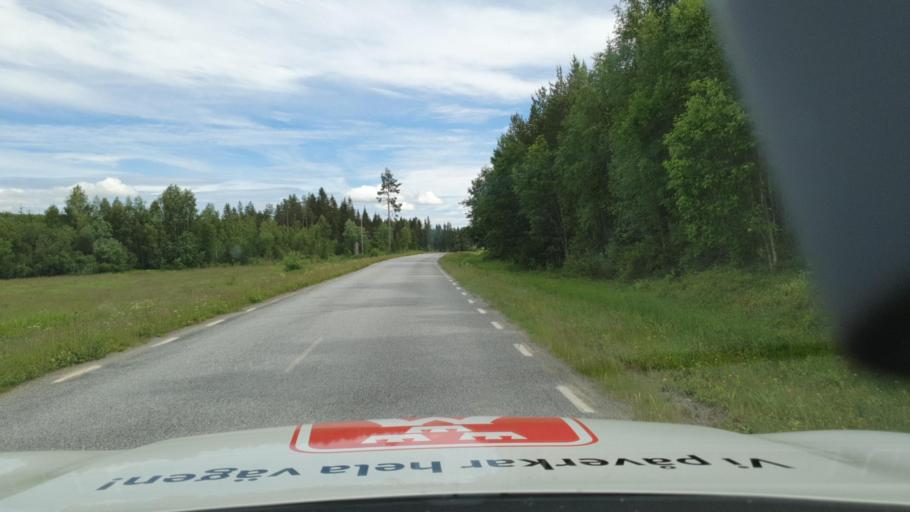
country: SE
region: Vaesterbotten
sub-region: Skelleftea Kommun
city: Soedra Bergsbyn
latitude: 64.5147
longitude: 20.9915
